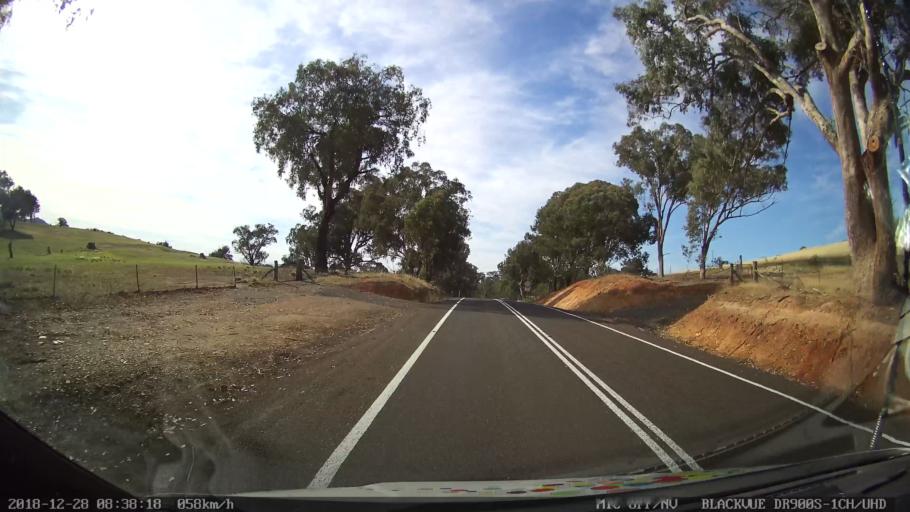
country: AU
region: New South Wales
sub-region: Blayney
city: Blayney
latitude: -34.0025
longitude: 149.3148
